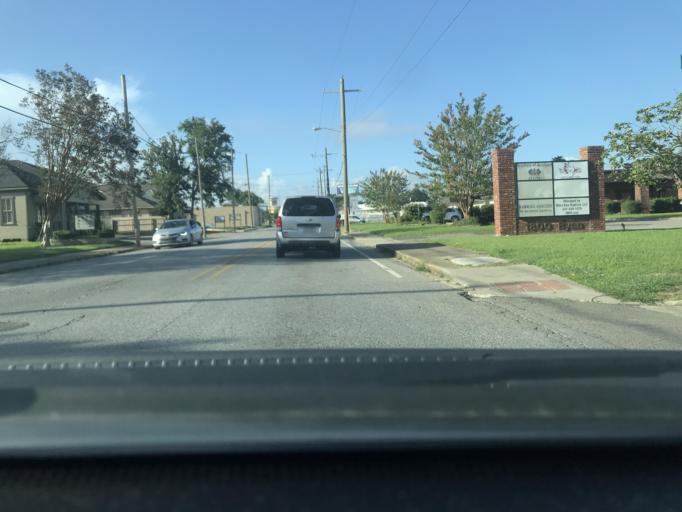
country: US
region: Louisiana
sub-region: Calcasieu Parish
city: Lake Charles
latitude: 30.2154
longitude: -93.2192
